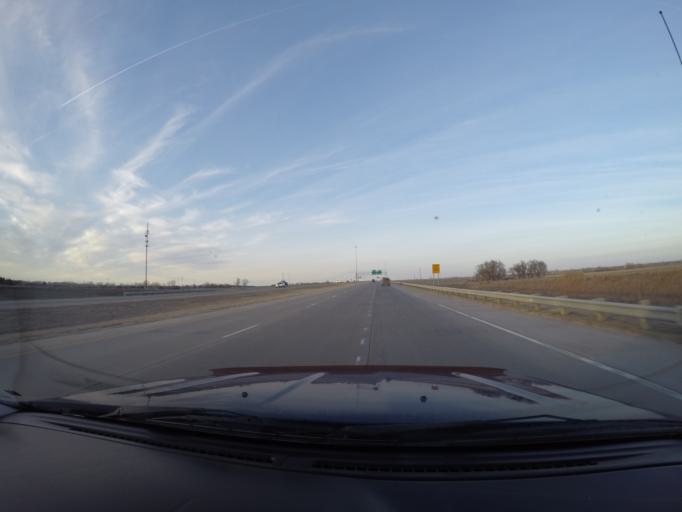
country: US
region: Kansas
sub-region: Saline County
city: Salina
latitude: 38.8689
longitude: -97.6453
